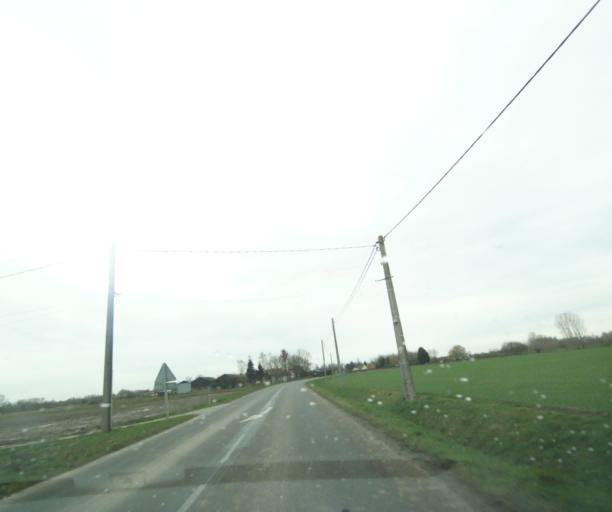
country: FR
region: Nord-Pas-de-Calais
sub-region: Departement du Nord
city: Crespin
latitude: 50.4329
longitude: 3.6619
